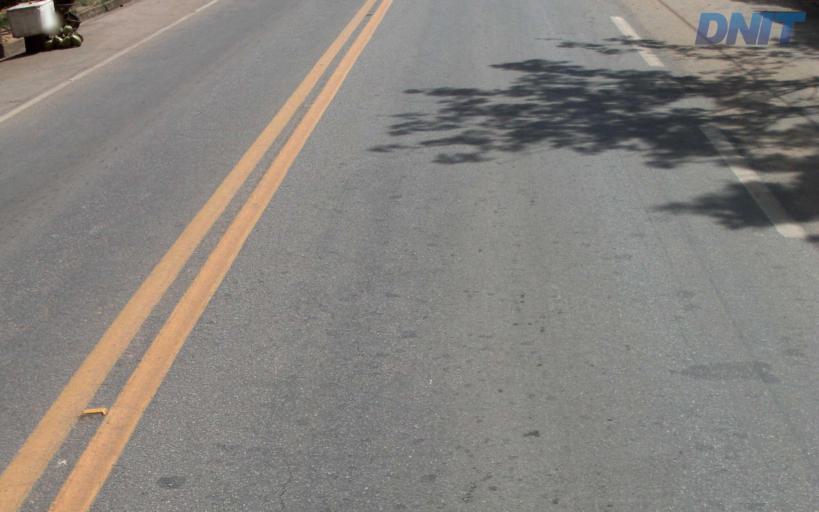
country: BR
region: Minas Gerais
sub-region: Belo Oriente
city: Belo Oriente
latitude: -19.1538
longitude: -42.2355
